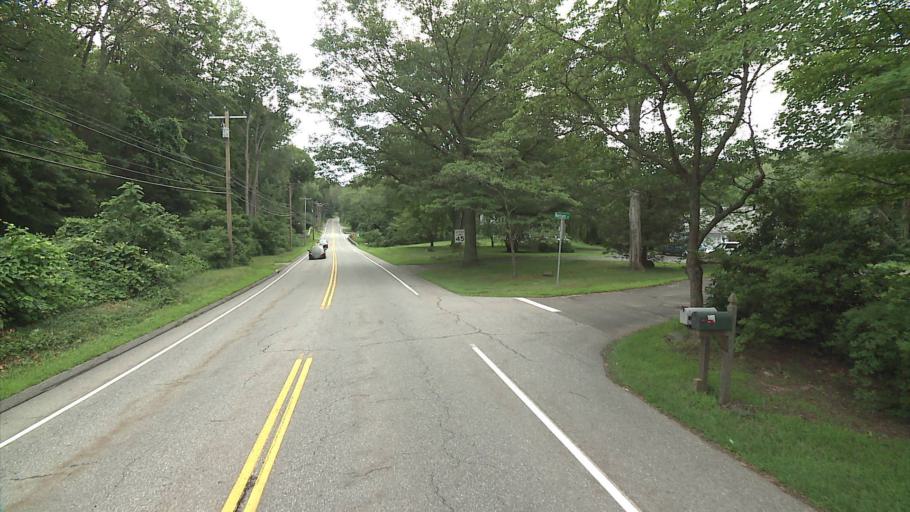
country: US
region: Connecticut
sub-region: Middlesex County
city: Higganum
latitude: 41.4829
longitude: -72.5567
